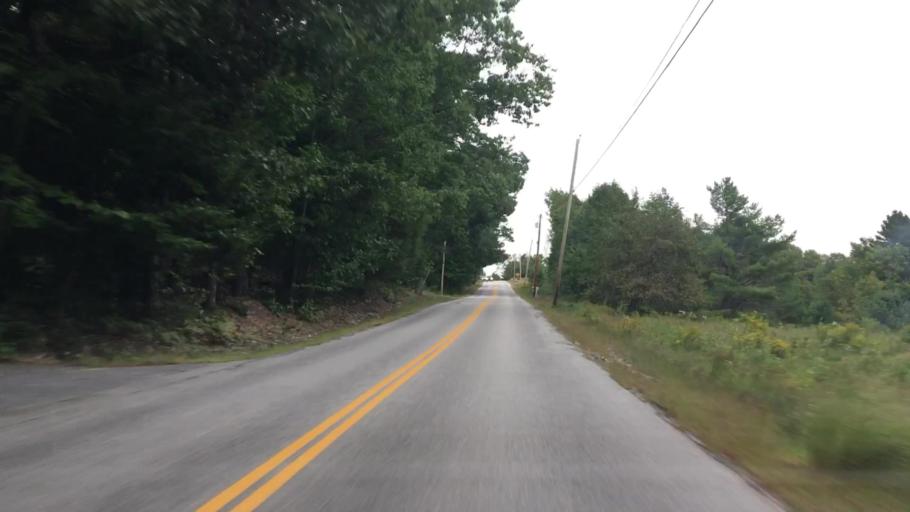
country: US
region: Maine
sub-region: Cumberland County
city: New Gloucester
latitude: 43.9076
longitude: -70.2288
